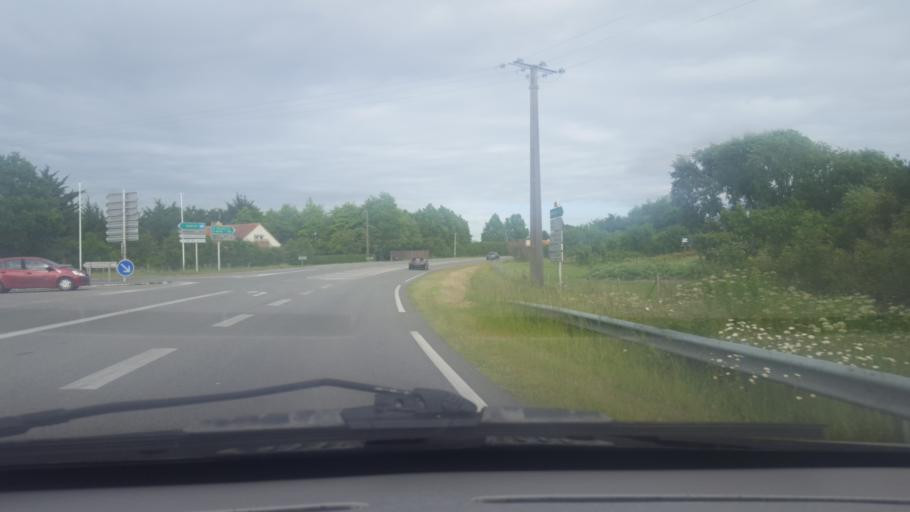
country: FR
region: Pays de la Loire
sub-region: Departement de la Loire-Atlantique
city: Bourgneuf-en-Retz
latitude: 47.0396
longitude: -1.9455
